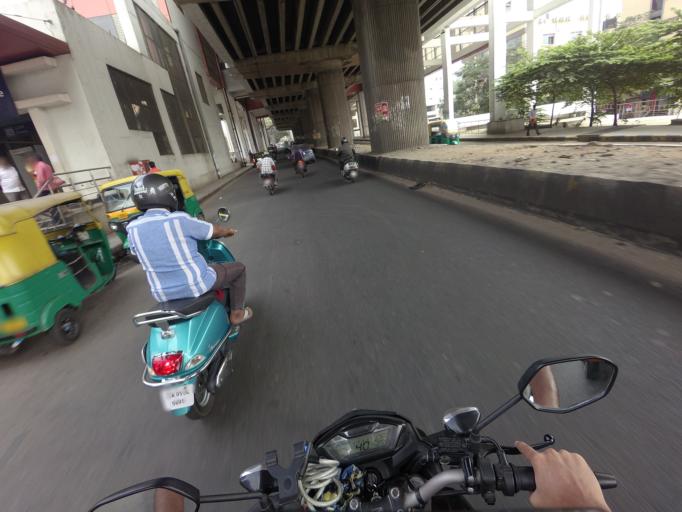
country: IN
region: Karnataka
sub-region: Bangalore Urban
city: Bangalore
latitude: 12.9615
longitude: 77.5334
